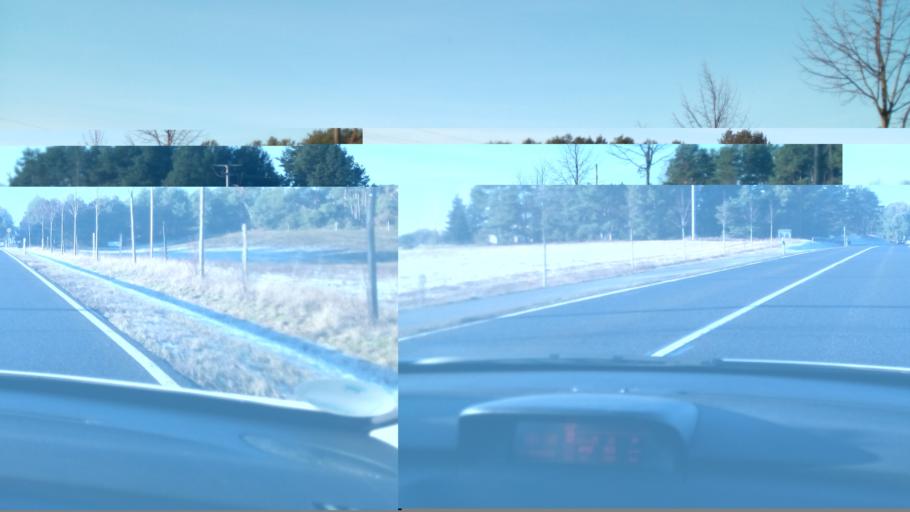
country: DE
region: Mecklenburg-Vorpommern
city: Neustrelitz
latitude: 53.3007
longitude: 13.0836
